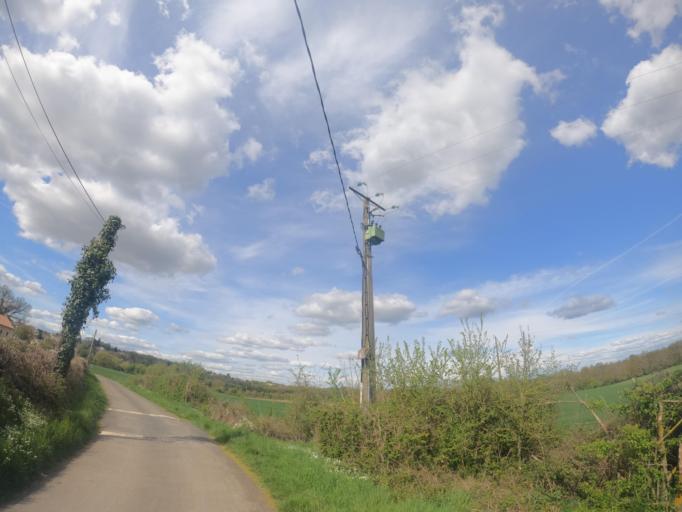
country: FR
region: Poitou-Charentes
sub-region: Departement des Deux-Sevres
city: Saint-Jean-de-Thouars
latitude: 46.9201
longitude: -0.1909
